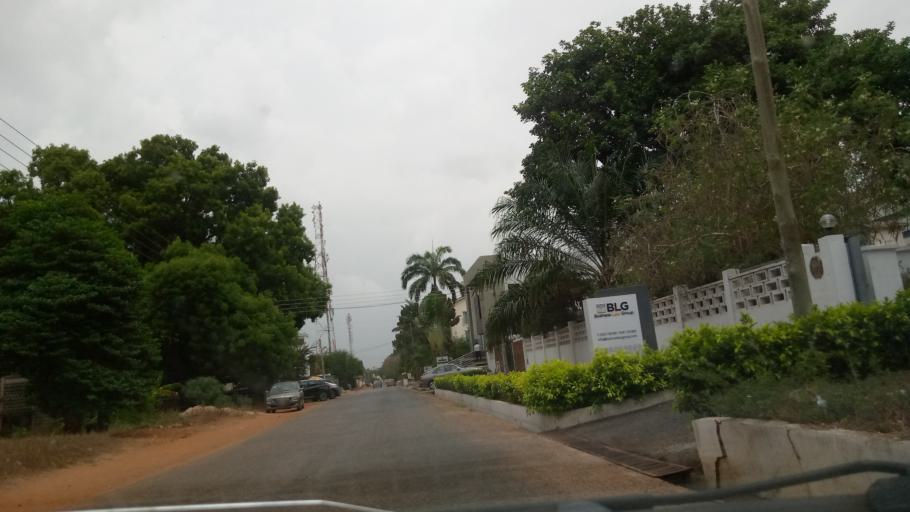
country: GH
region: Greater Accra
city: Accra
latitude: 5.6072
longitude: -0.1868
